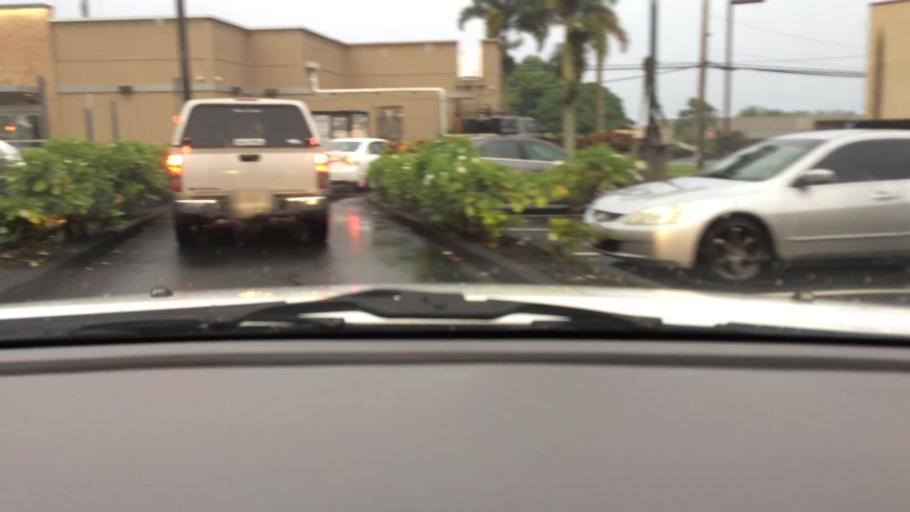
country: US
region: Hawaii
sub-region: Hawaii County
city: Kea'au
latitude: 19.6217
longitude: -155.0395
